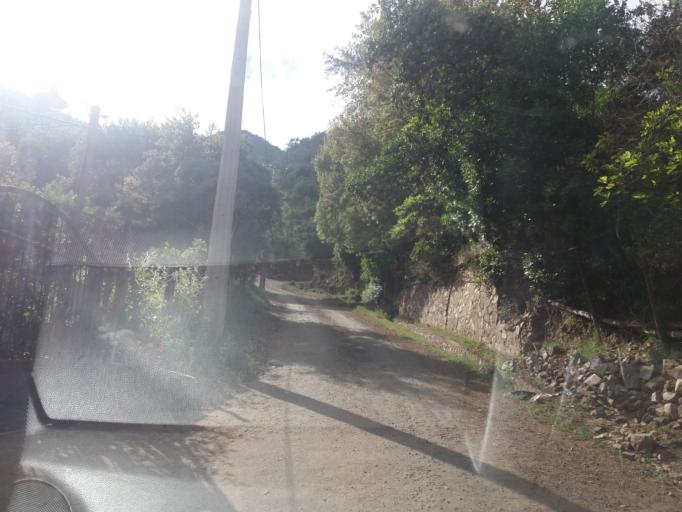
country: CL
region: Valparaiso
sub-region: Provincia de Marga Marga
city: Limache
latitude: -33.0707
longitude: -71.0622
